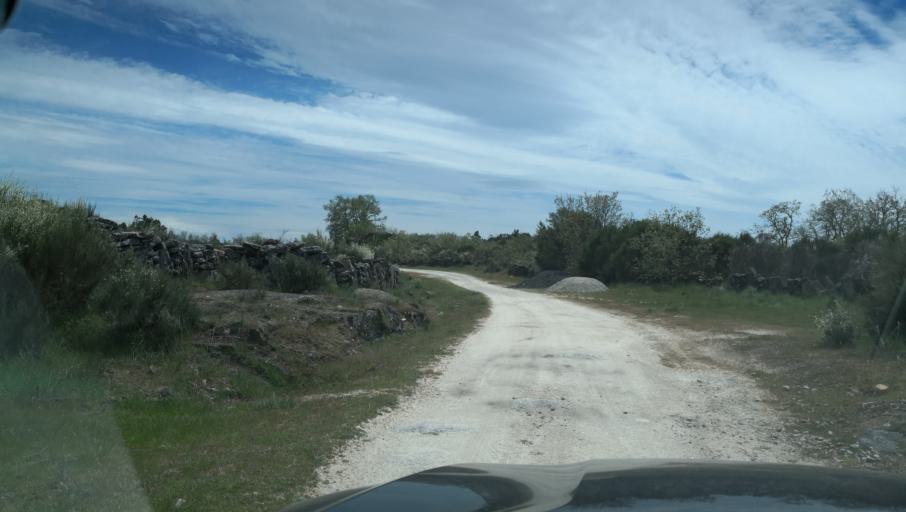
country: PT
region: Vila Real
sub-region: Vila Real
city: Vila Real
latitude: 41.3786
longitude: -7.6604
